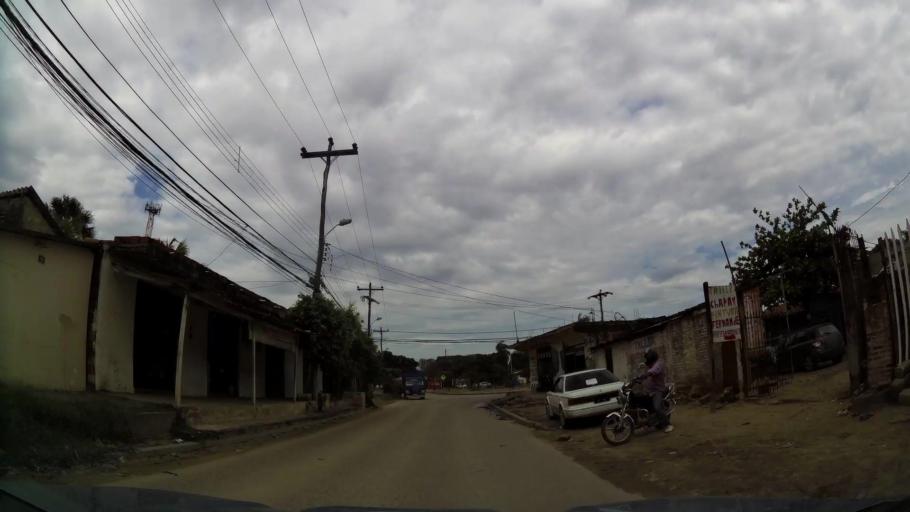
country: BO
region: Santa Cruz
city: Santa Cruz de la Sierra
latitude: -17.7408
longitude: -63.1807
